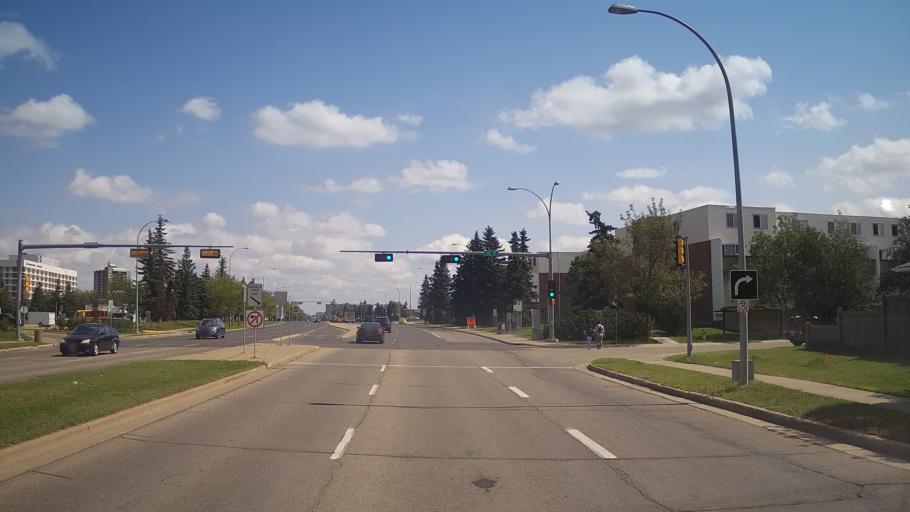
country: CA
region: Alberta
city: St. Albert
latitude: 53.5197
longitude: -113.6194
